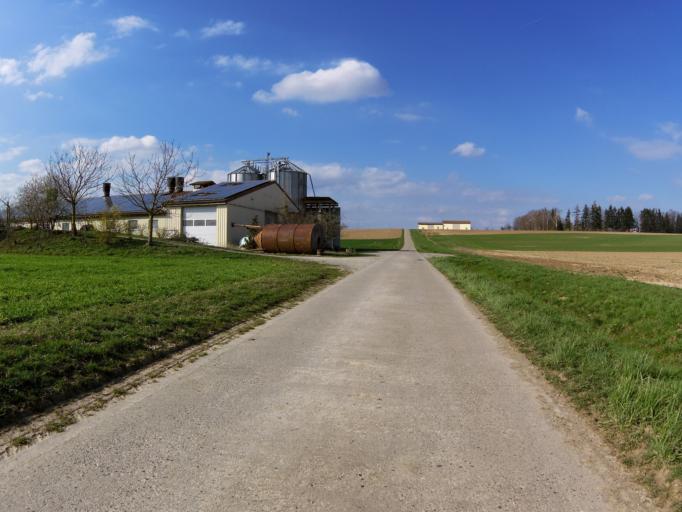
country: DE
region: Bavaria
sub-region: Regierungsbezirk Unterfranken
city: Biebelried
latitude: 49.7915
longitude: 10.0803
